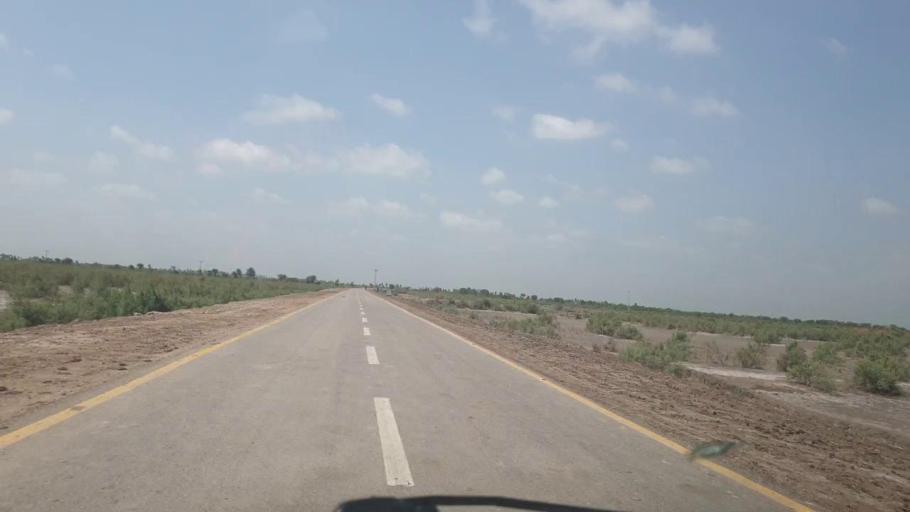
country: PK
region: Sindh
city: Berani
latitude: 25.6995
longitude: 68.9334
